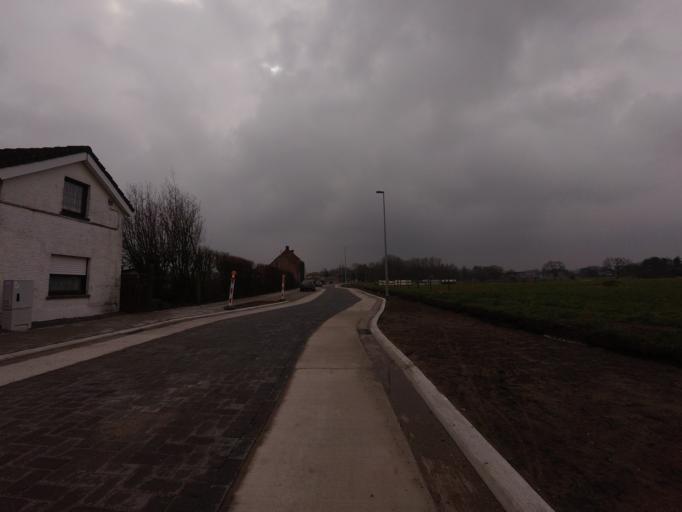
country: BE
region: Flanders
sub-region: Provincie Antwerpen
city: Sint-Katelijne-Waver
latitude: 51.0598
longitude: 4.5692
